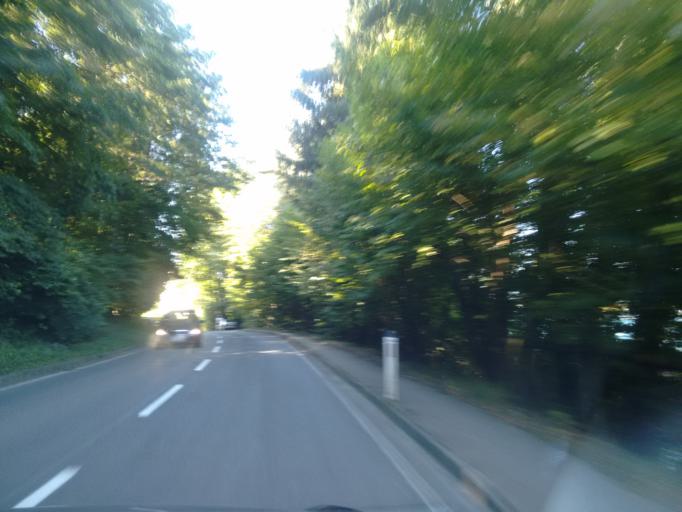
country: AT
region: Upper Austria
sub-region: Politischer Bezirk Vocklabruck
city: Attersee
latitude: 47.8910
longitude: 13.5685
